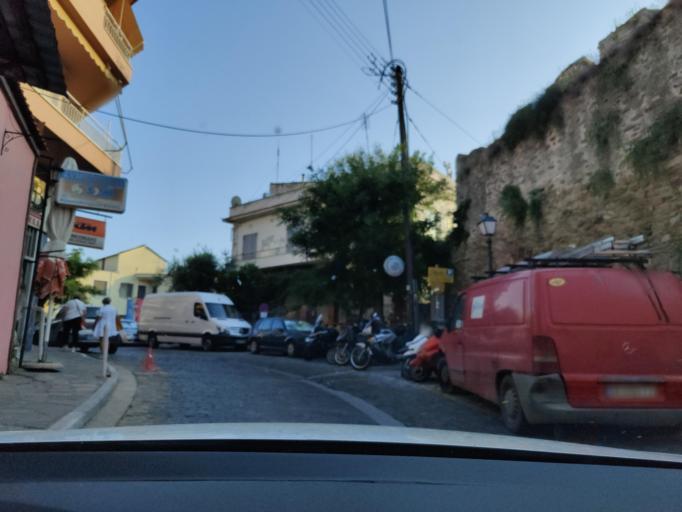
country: GR
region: East Macedonia and Thrace
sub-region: Nomos Kavalas
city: Kavala
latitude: 40.9347
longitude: 24.4134
